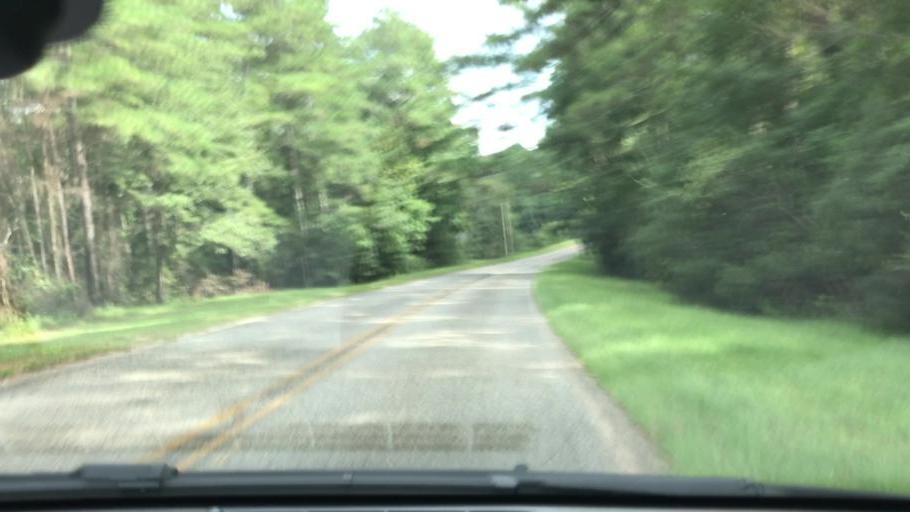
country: US
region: Georgia
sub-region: Early County
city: Blakely
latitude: 31.5032
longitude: -84.9439
